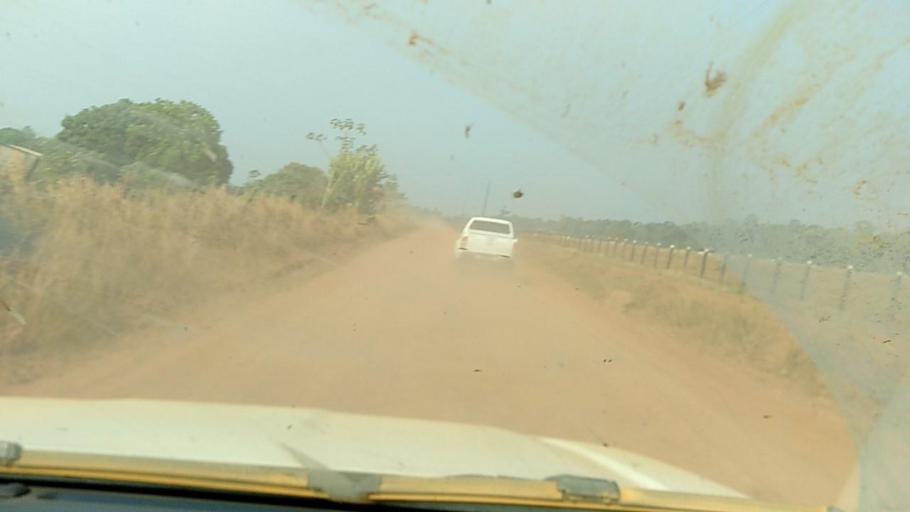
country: BR
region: Rondonia
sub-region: Porto Velho
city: Porto Velho
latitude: -8.7766
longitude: -64.0833
